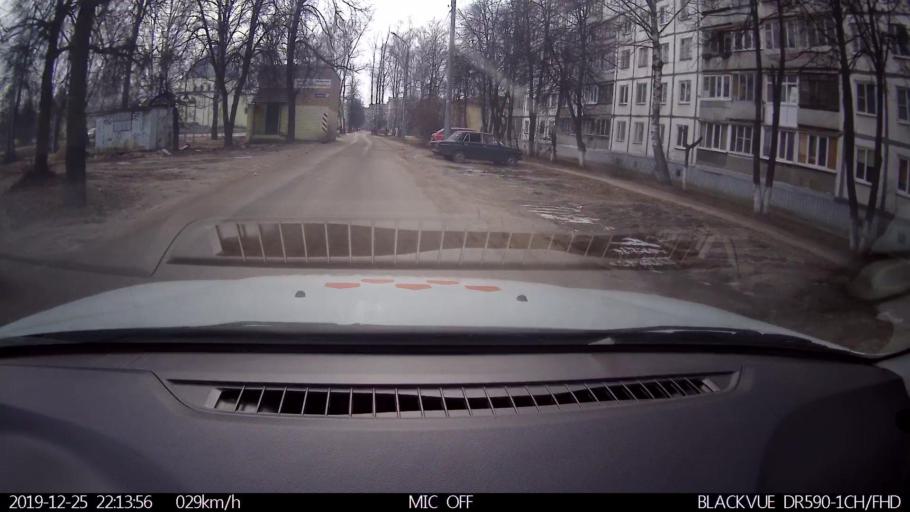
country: RU
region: Nizjnij Novgorod
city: Gorbatovka
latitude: 56.3332
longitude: 43.8468
